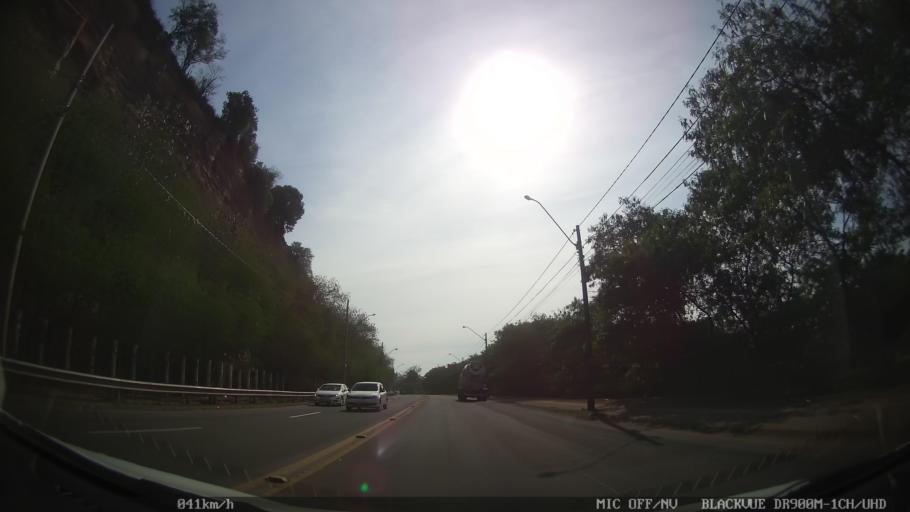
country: BR
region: Sao Paulo
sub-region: Piracicaba
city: Piracicaba
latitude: -22.7138
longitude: -47.6774
